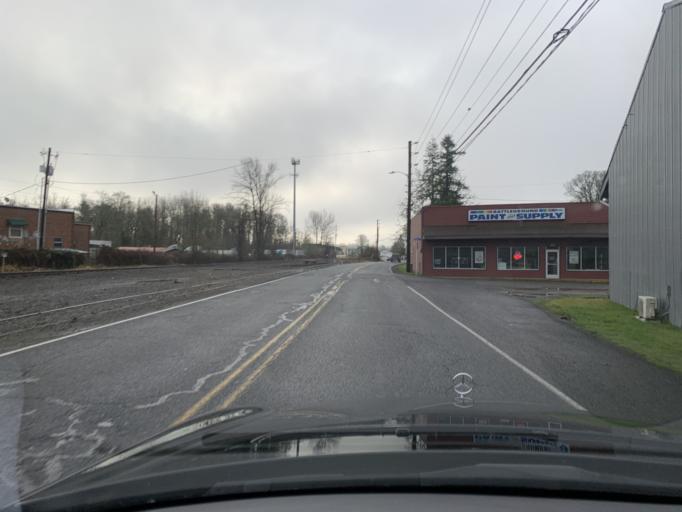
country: US
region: Washington
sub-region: Clark County
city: Battle Ground
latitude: 45.7799
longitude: -122.5283
